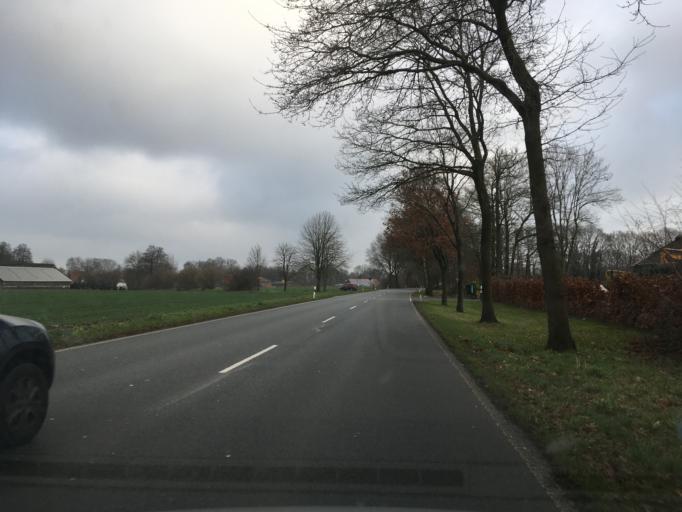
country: DE
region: North Rhine-Westphalia
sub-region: Regierungsbezirk Munster
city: Gronau
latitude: 52.2032
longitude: 7.0090
